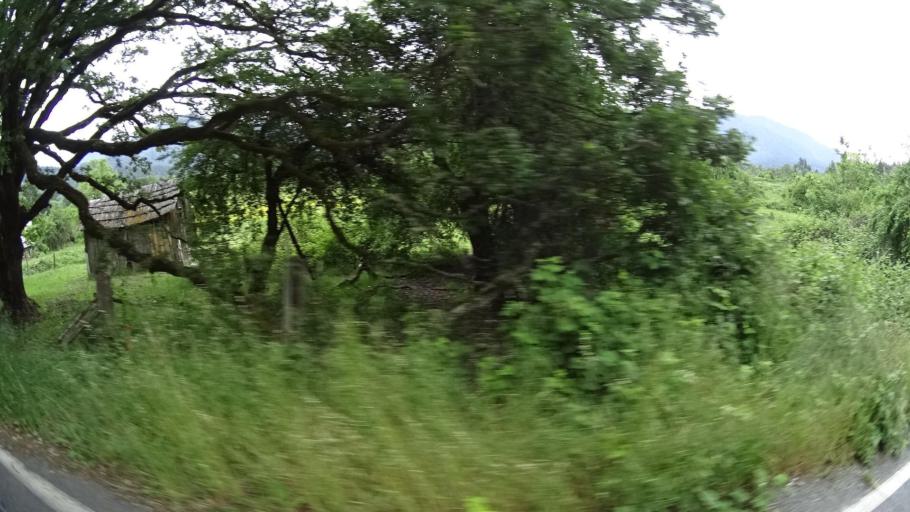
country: US
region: California
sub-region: Humboldt County
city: Willow Creek
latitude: 41.0912
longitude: -123.7132
